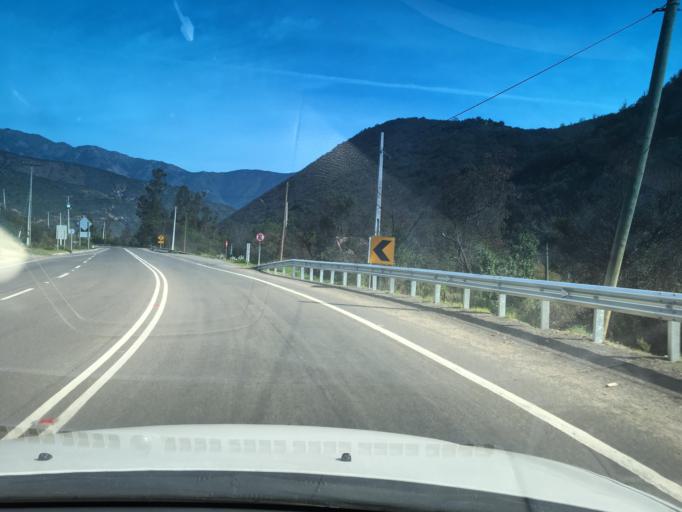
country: CL
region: Valparaiso
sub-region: Provincia de Marga Marga
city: Limache
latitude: -33.0595
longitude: -71.0544
